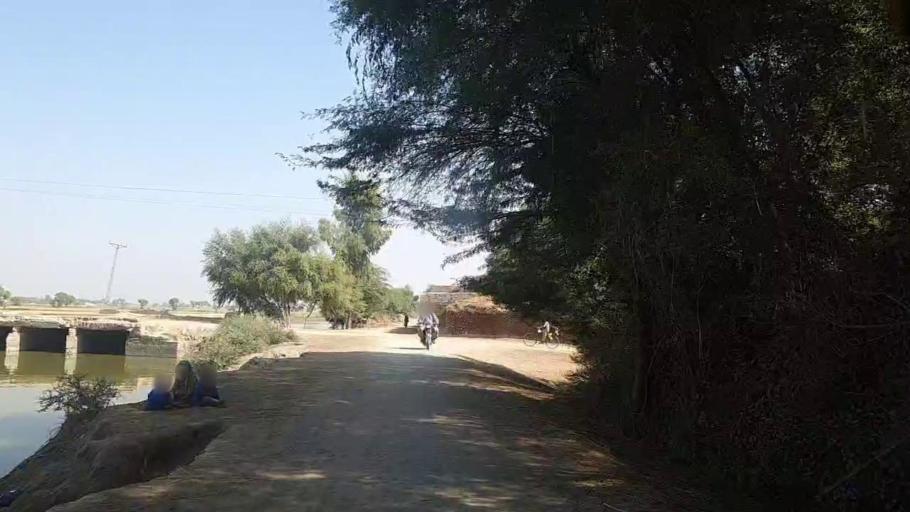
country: PK
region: Sindh
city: Thul
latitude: 28.2478
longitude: 68.8085
